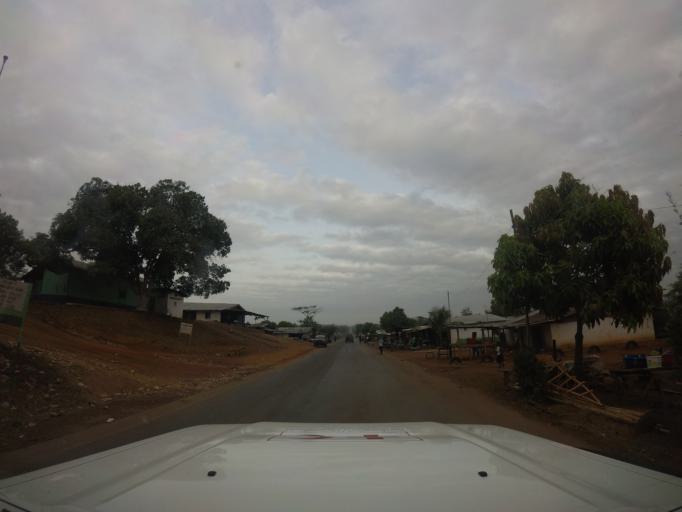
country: LR
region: Bomi
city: Tubmanburg
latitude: 6.7165
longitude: -10.9741
